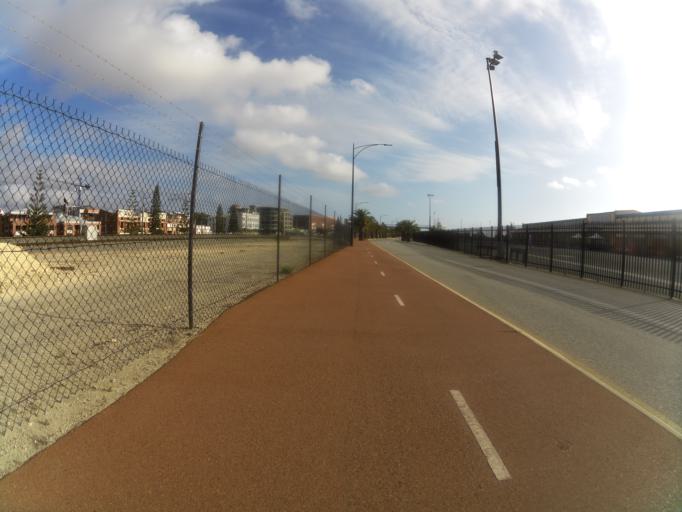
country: AU
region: Western Australia
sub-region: Fremantle
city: North Fremantle
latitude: -32.0471
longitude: 115.7494
